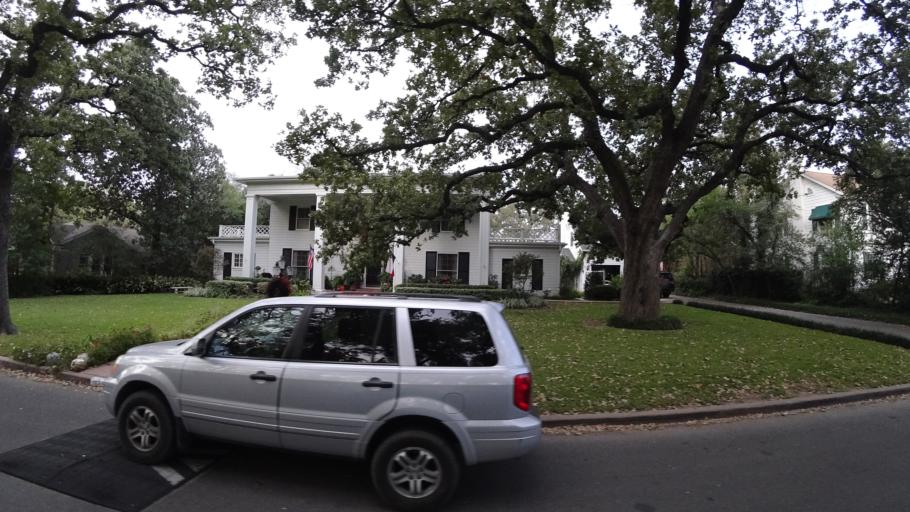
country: US
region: Texas
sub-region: Travis County
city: Austin
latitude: 30.2996
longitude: -97.7551
